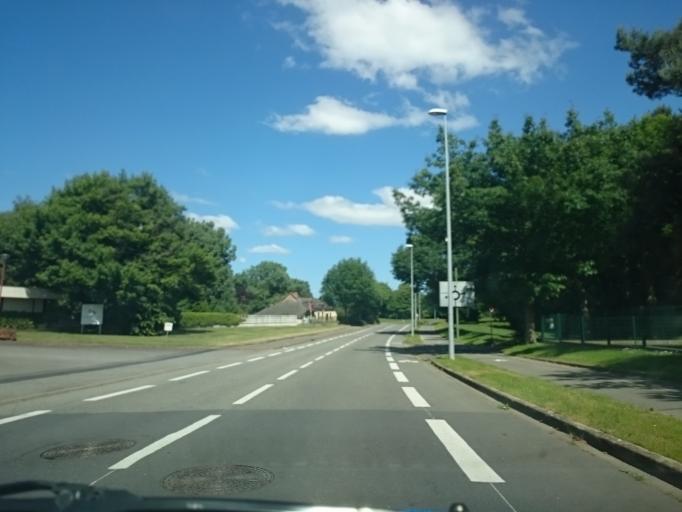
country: FR
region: Brittany
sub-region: Departement d'Ille-et-Vilaine
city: Cesson-Sevigne
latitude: 48.1233
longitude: -1.6236
